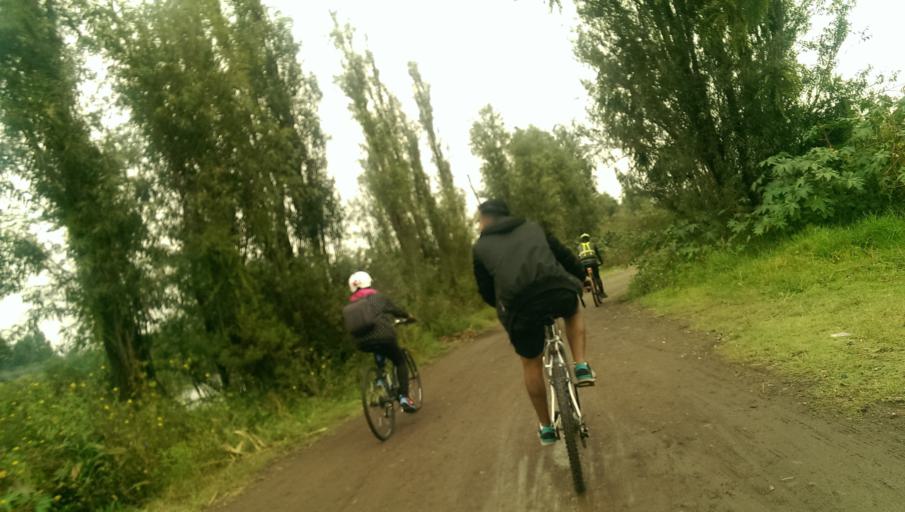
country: MX
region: Mexico City
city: Xochimilco
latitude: 19.2789
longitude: -99.0722
